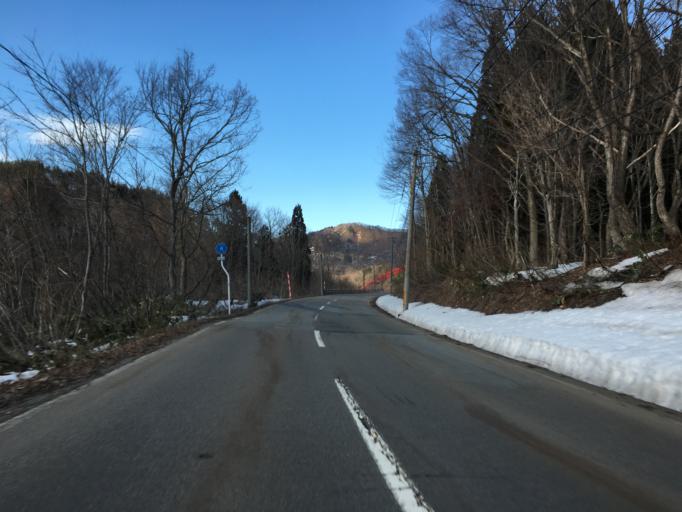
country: JP
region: Yamagata
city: Nagai
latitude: 37.9469
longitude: 139.9147
